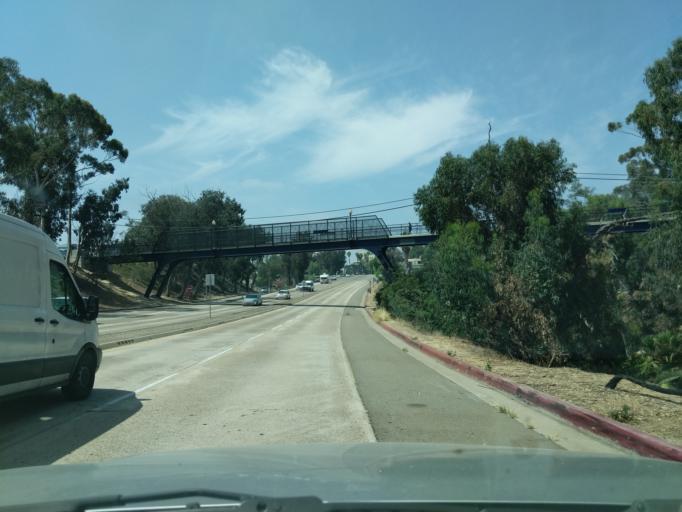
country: US
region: California
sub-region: San Diego County
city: San Diego
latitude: 32.7509
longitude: -117.1528
